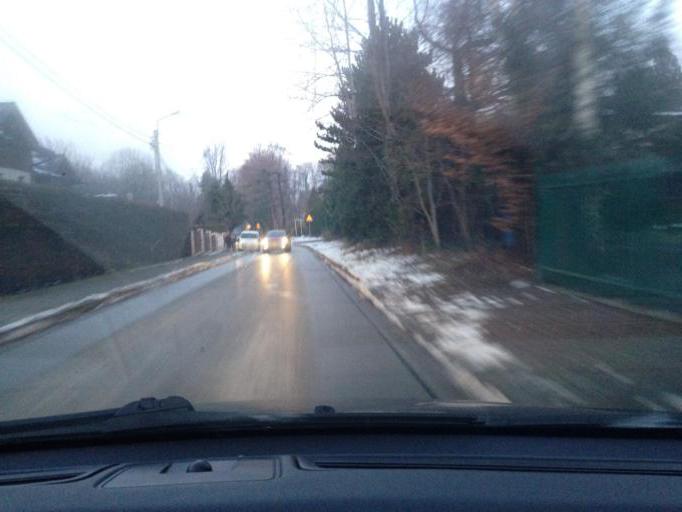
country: PL
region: Silesian Voivodeship
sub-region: Powiat bielski
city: Bystra
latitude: 49.7854
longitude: 19.0408
